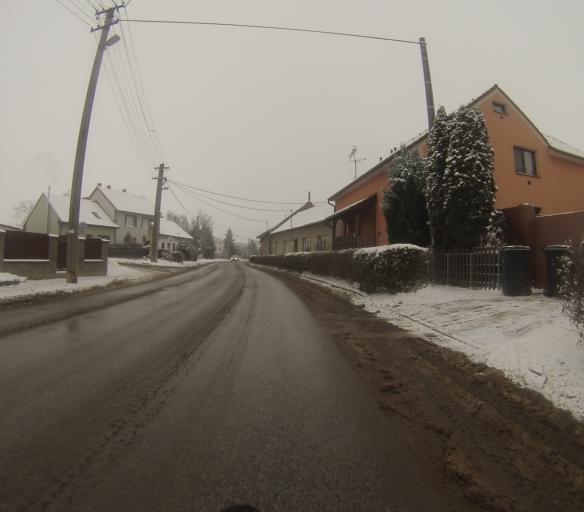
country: CZ
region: South Moravian
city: Troubsko
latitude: 49.1686
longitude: 16.5125
